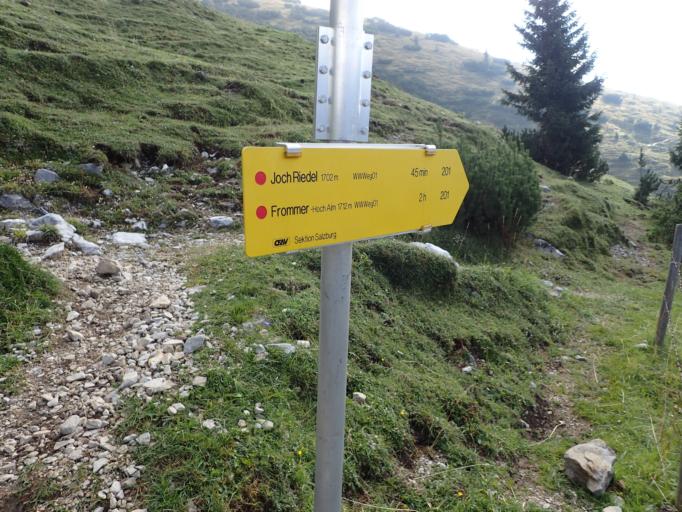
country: AT
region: Salzburg
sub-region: Politischer Bezirk Sankt Johann im Pongau
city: Werfenweng
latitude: 47.4843
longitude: 13.2902
